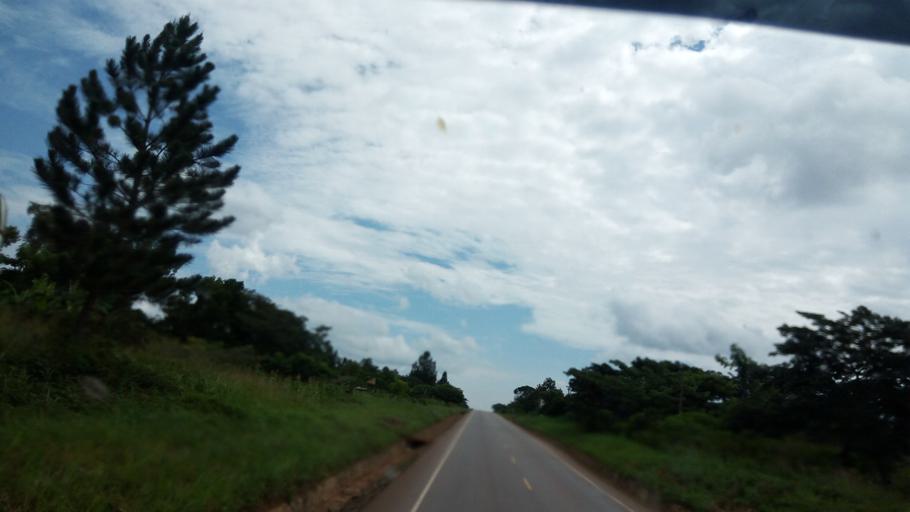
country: UG
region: Central Region
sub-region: Nakasongola District
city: Nakasongola
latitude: 1.1202
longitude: 32.4655
